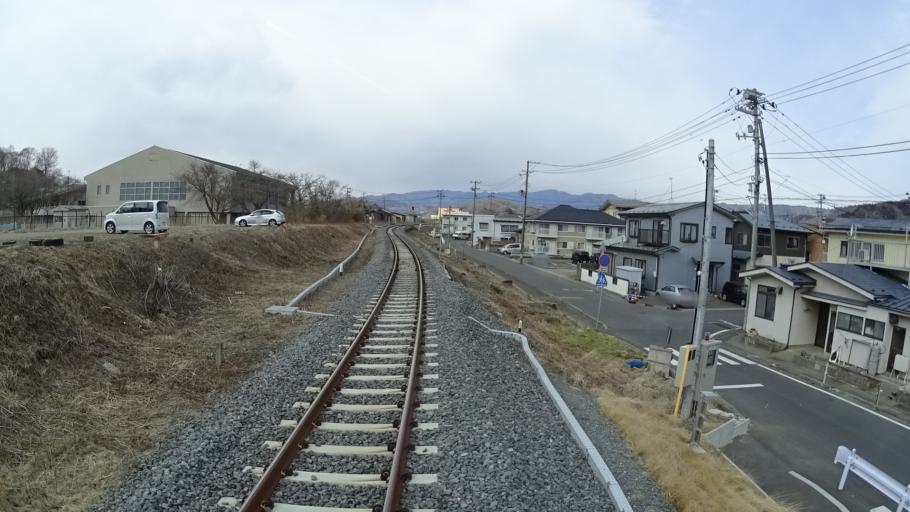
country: JP
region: Iwate
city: Miyako
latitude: 39.6371
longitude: 141.9585
